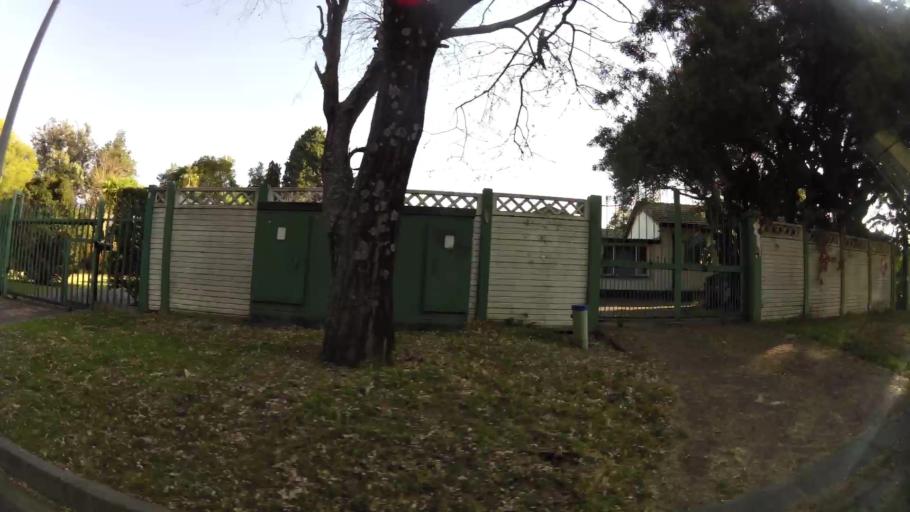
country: ZA
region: Gauteng
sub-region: City of Johannesburg Metropolitan Municipality
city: Modderfontein
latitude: -26.1311
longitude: 28.1034
